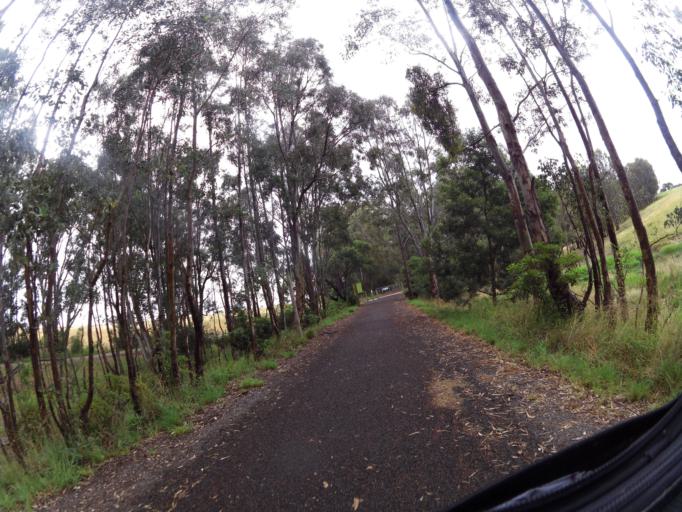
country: AU
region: Victoria
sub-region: East Gippsland
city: Bairnsdale
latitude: -37.8182
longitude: 147.7270
